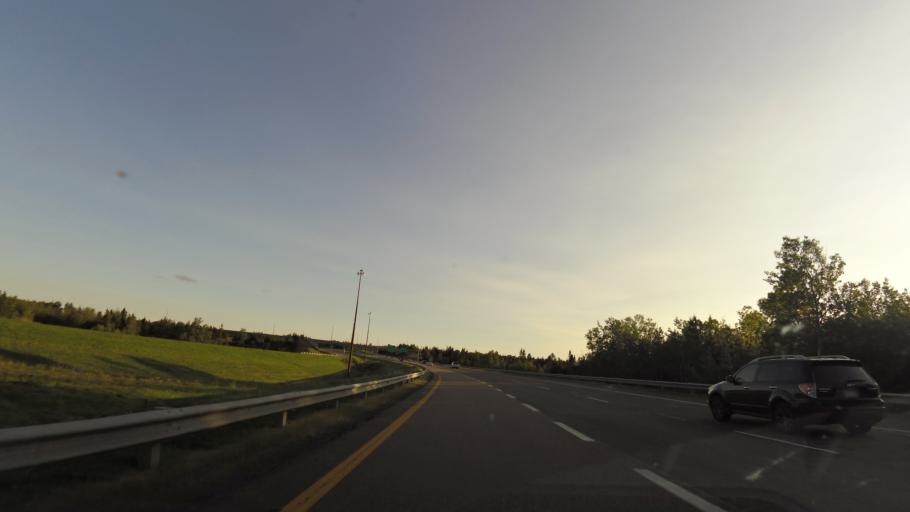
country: CA
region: New Brunswick
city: Salisbury
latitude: 45.9969
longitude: -65.1379
